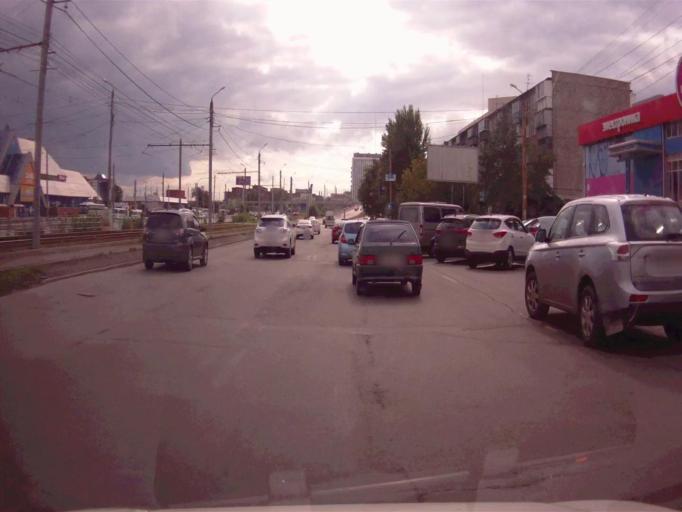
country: RU
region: Chelyabinsk
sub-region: Gorod Chelyabinsk
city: Chelyabinsk
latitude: 55.1414
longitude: 61.4124
